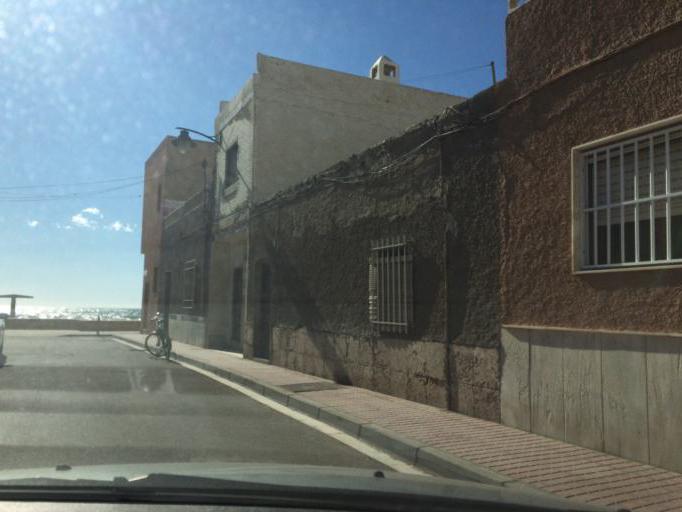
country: ES
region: Andalusia
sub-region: Provincia de Almeria
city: Retamar
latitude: 36.7800
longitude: -2.2442
